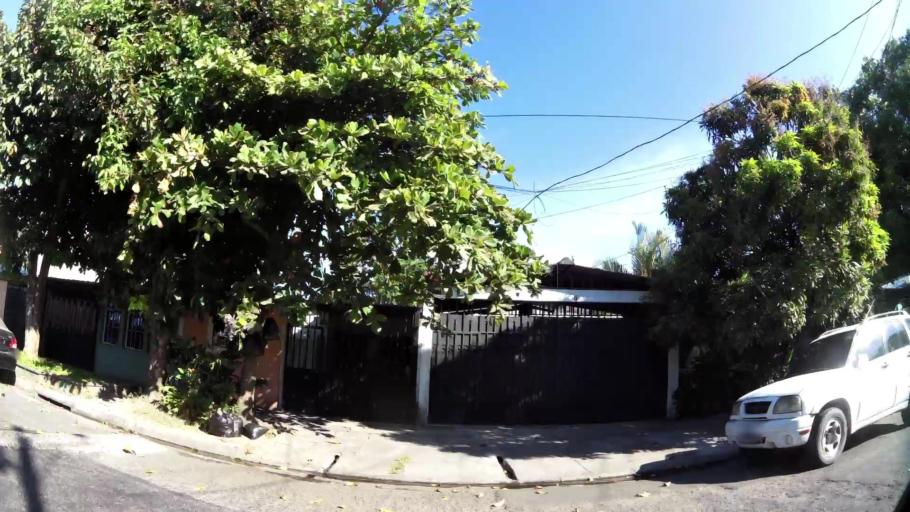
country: SV
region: La Libertad
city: Santa Tecla
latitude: 13.6873
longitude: -89.2920
